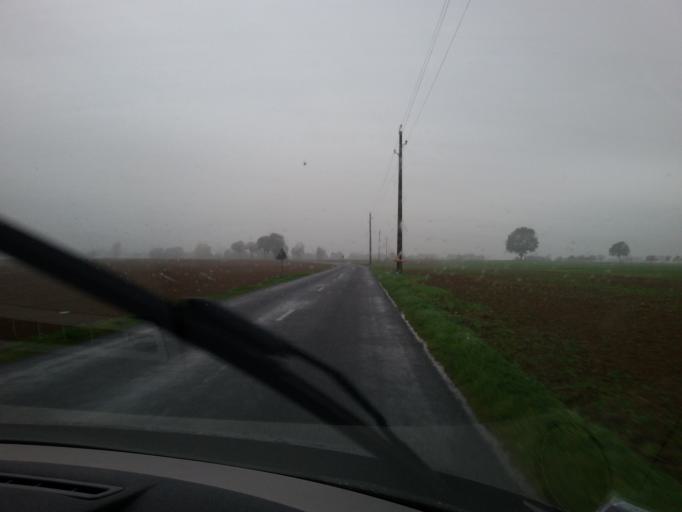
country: FR
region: Haute-Normandie
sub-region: Departement de l'Eure
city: Beuzeville
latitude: 49.4239
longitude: 0.3790
